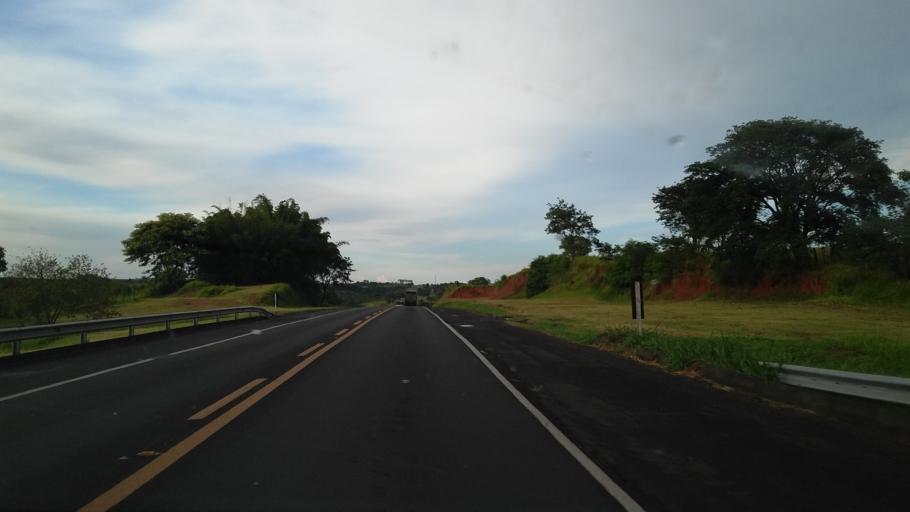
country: BR
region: Sao Paulo
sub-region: Marilia
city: Marilia
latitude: -21.9397
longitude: -49.9201
